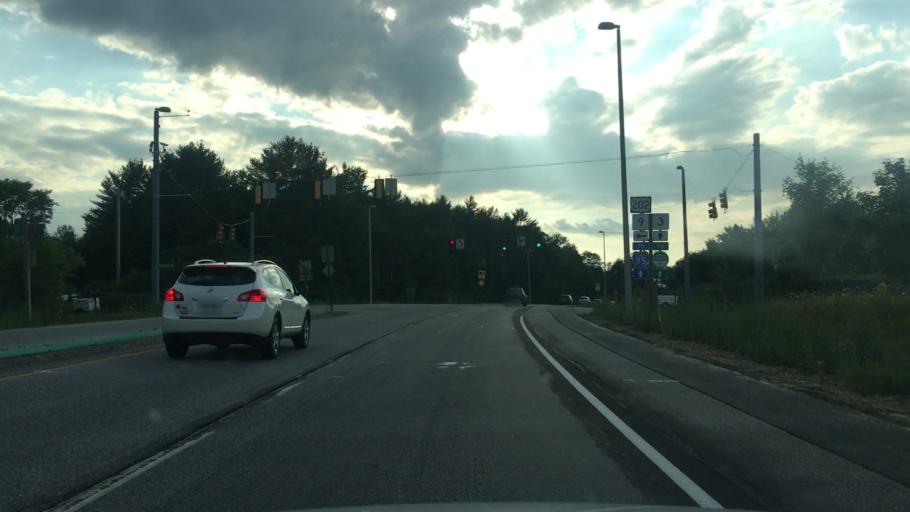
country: US
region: Maine
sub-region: Kennebec County
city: Augusta
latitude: 44.3279
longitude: -69.7448
